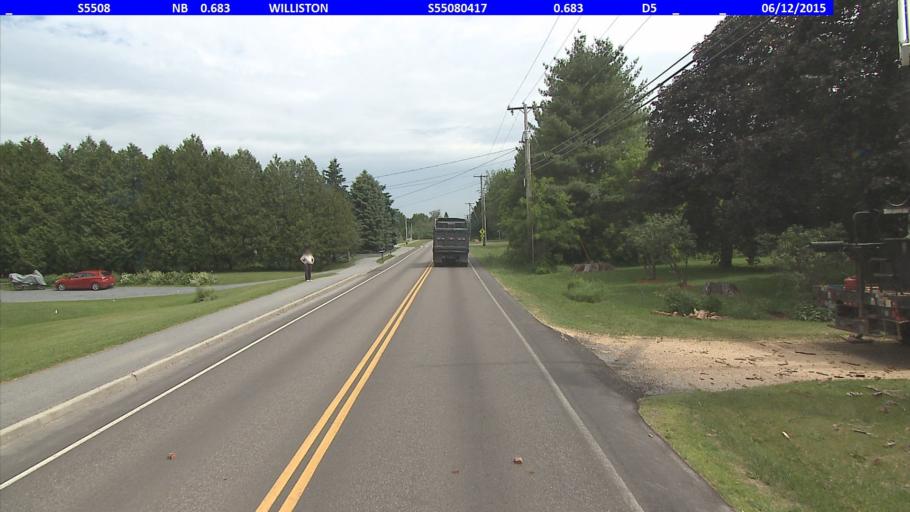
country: US
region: Vermont
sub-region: Chittenden County
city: Williston
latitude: 44.4464
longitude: -73.0625
